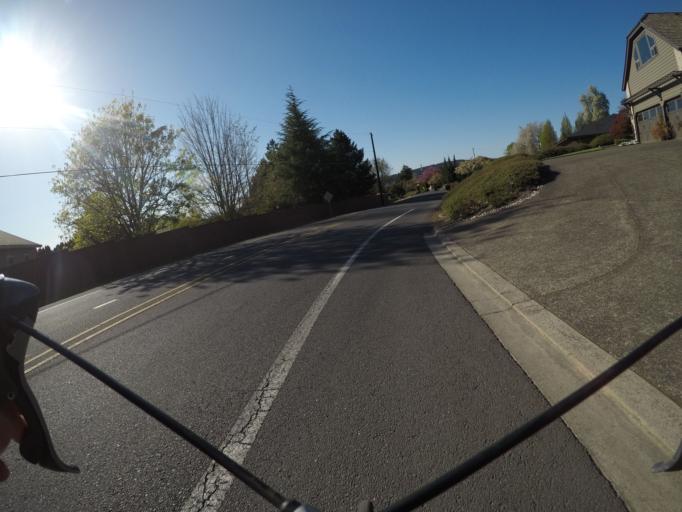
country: US
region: Oregon
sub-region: Washington County
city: King City
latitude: 45.4165
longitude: -122.8368
